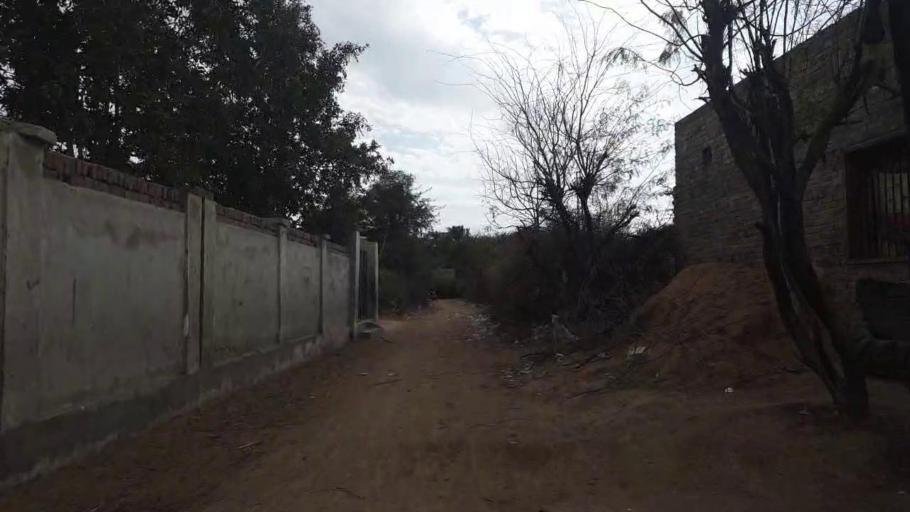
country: PK
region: Sindh
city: Hala
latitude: 25.9300
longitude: 68.4534
